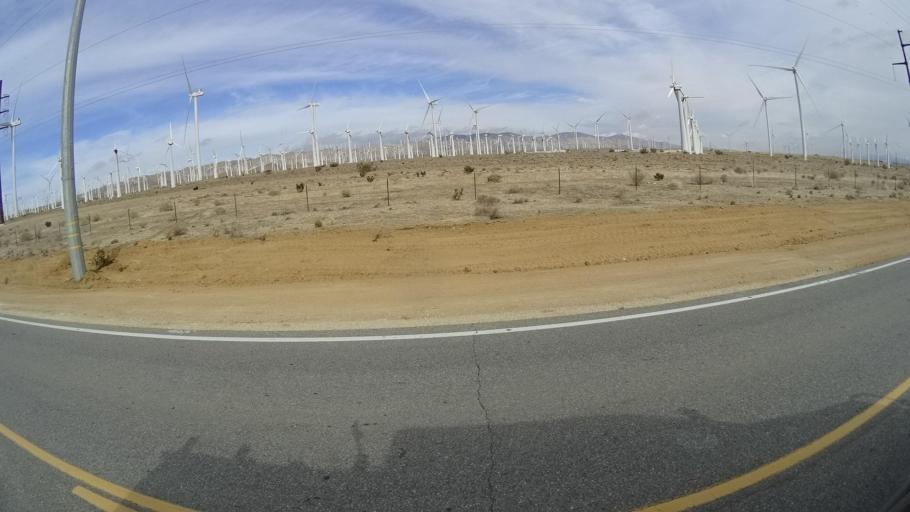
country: US
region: California
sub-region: Kern County
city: Mojave
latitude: 35.0385
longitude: -118.2643
